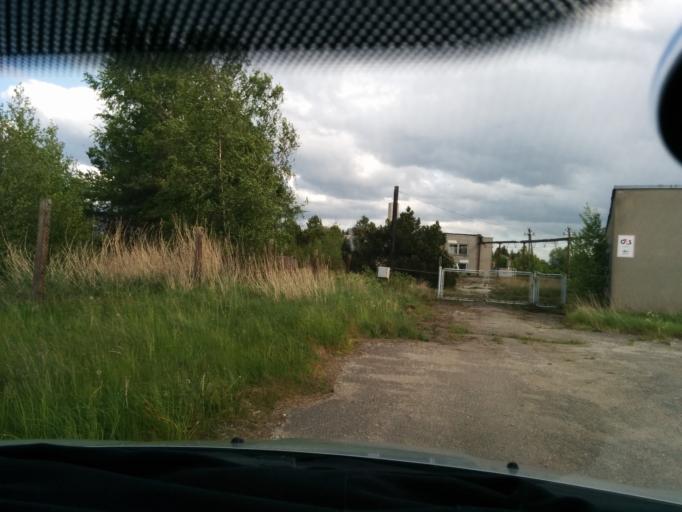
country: EE
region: Harju
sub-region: Loksa linn
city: Loksa
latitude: 59.6551
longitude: 25.6725
